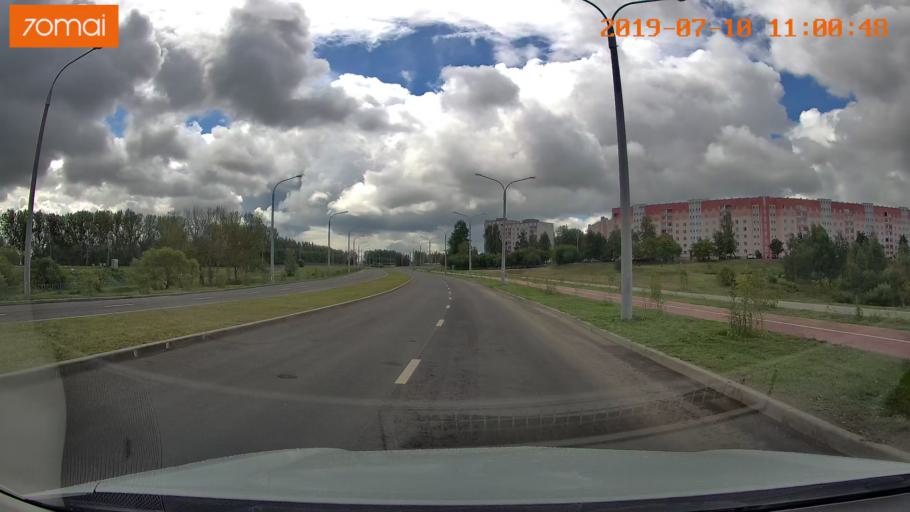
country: BY
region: Minsk
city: Syenitsa
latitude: 53.8561
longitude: 27.5560
